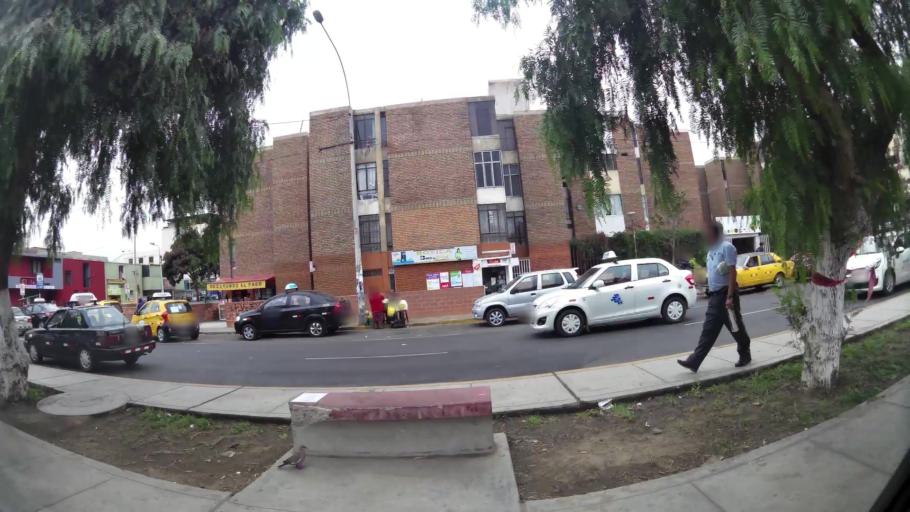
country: PE
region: La Libertad
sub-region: Provincia de Trujillo
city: Trujillo
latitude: -8.1123
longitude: -79.0349
